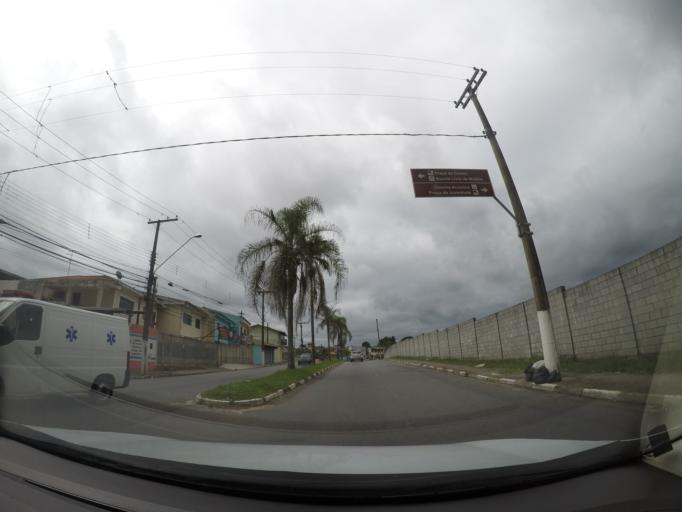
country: BR
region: Sao Paulo
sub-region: Aruja
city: Aruja
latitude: -23.3888
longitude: -46.3118
